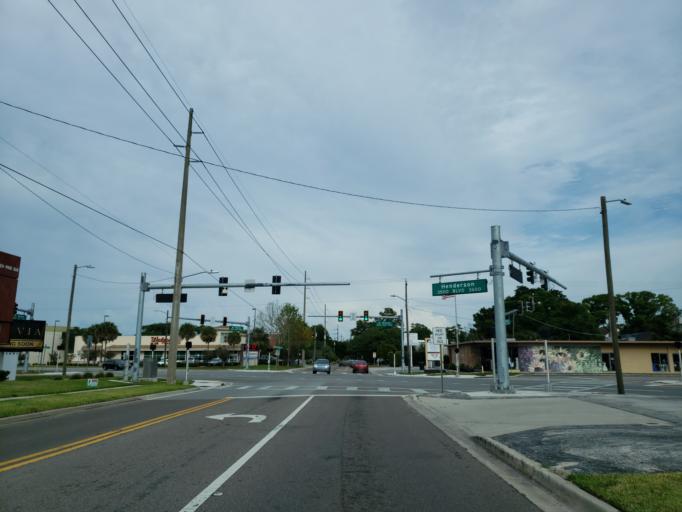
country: US
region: Florida
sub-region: Hillsborough County
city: Tampa
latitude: 27.9375
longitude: -82.5022
